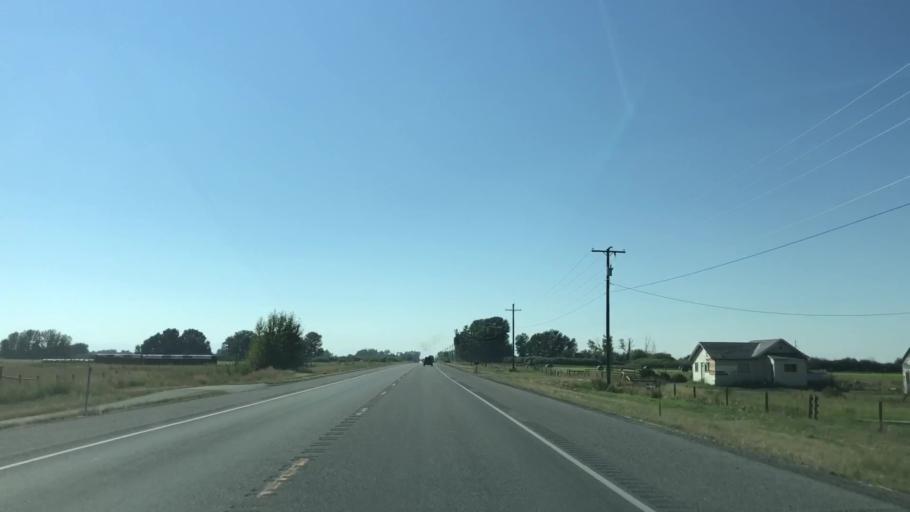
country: US
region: Montana
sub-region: Gallatin County
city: Belgrade
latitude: 45.7292
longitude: -111.1475
